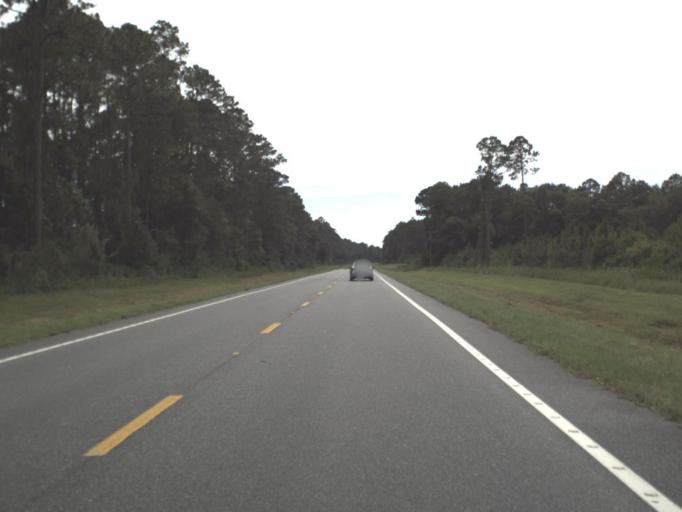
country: US
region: Florida
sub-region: Taylor County
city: Perry
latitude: 30.1059
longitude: -83.4317
